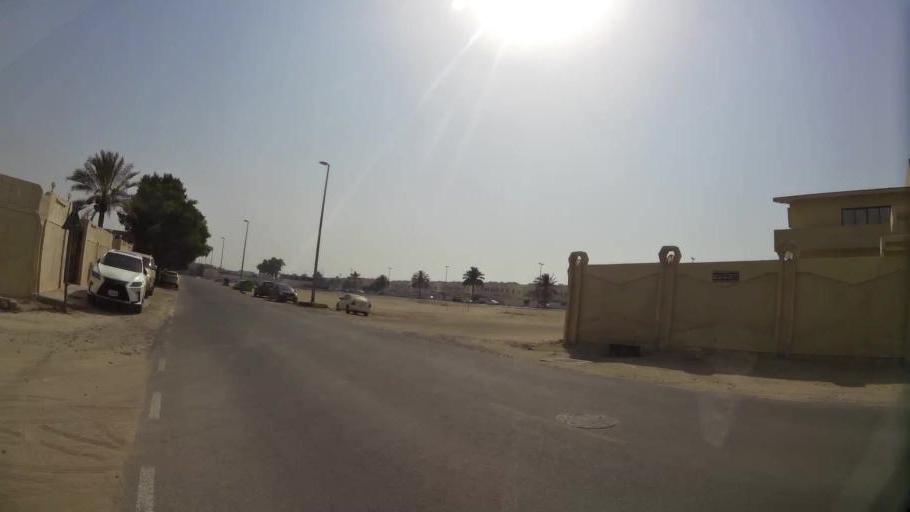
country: AE
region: Ajman
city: Ajman
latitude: 25.3910
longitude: 55.4249
